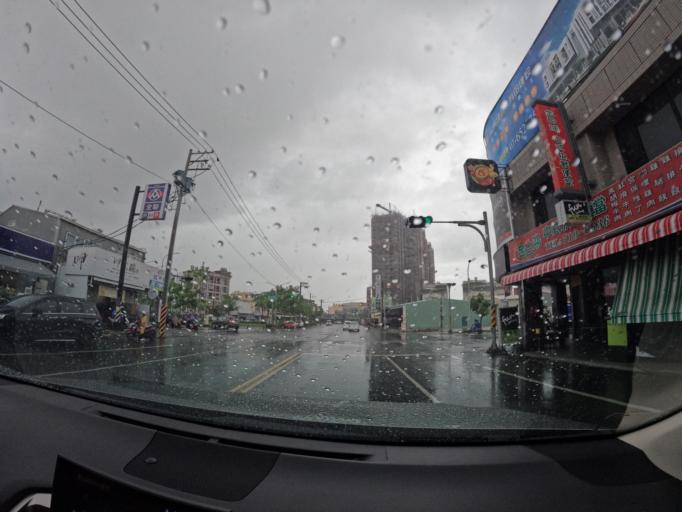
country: TW
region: Taiwan
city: Fengshan
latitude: 22.6403
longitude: 120.3645
